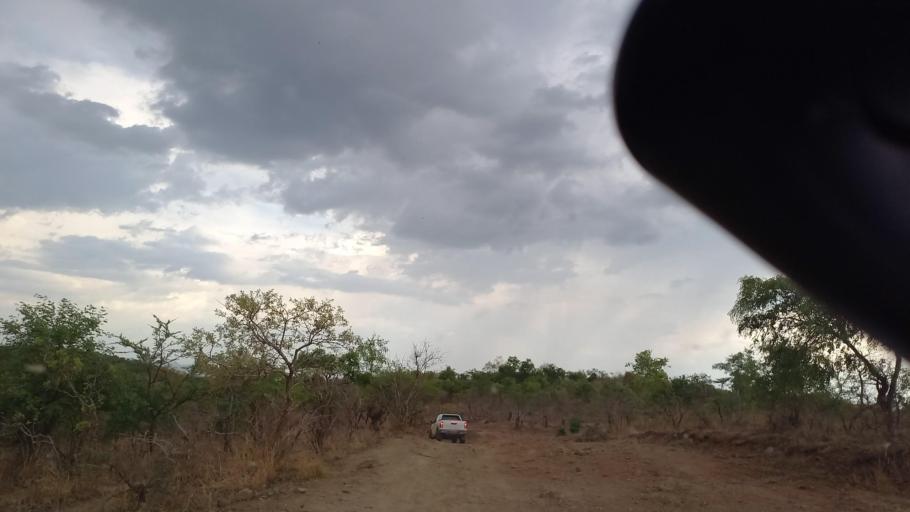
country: ZM
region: Lusaka
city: Kafue
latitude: -16.1214
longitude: 28.0626
